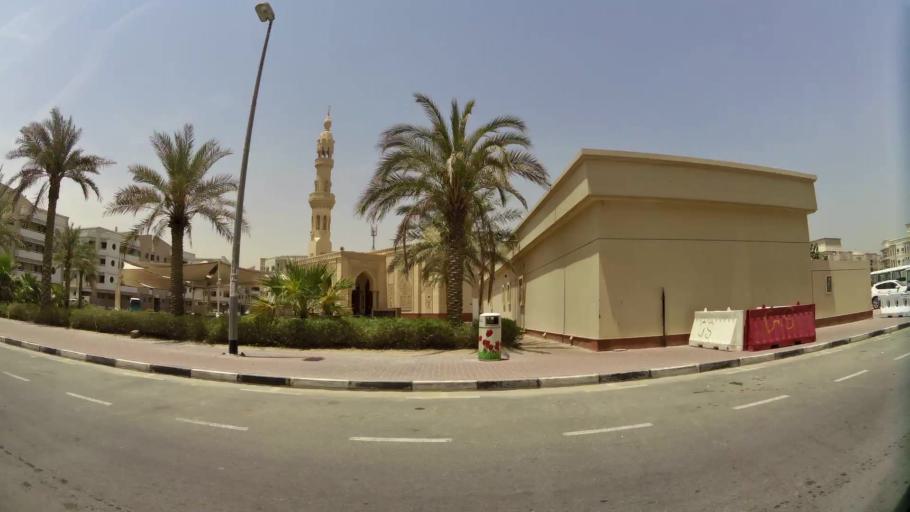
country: AE
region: Ash Shariqah
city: Sharjah
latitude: 25.2780
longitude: 55.4120
